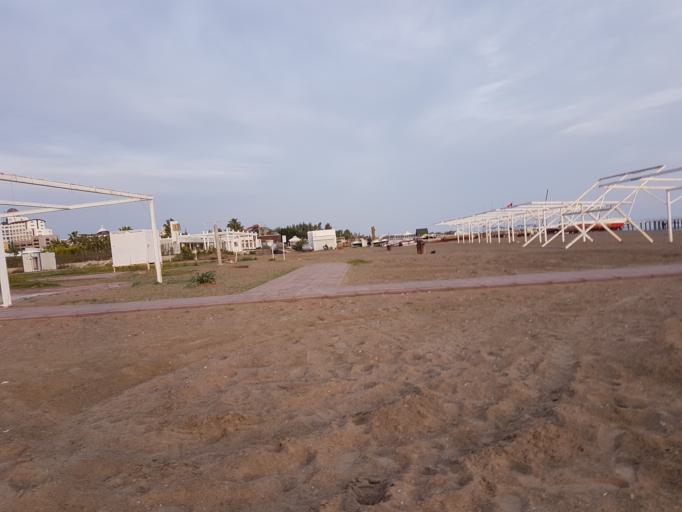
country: TR
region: Antalya
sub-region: Serik
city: Kumkoey
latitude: 36.8535
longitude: 30.8867
